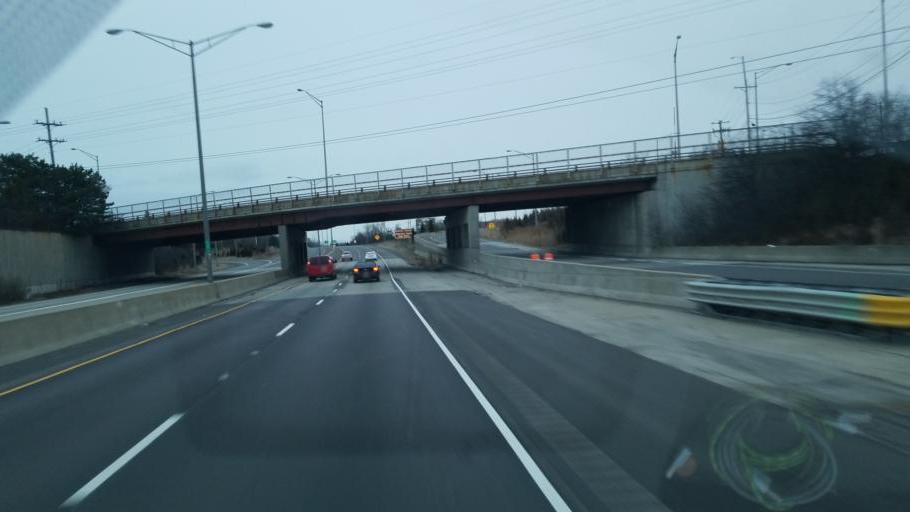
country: US
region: Illinois
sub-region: Lake County
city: Highland Park
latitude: 42.1604
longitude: -87.8067
